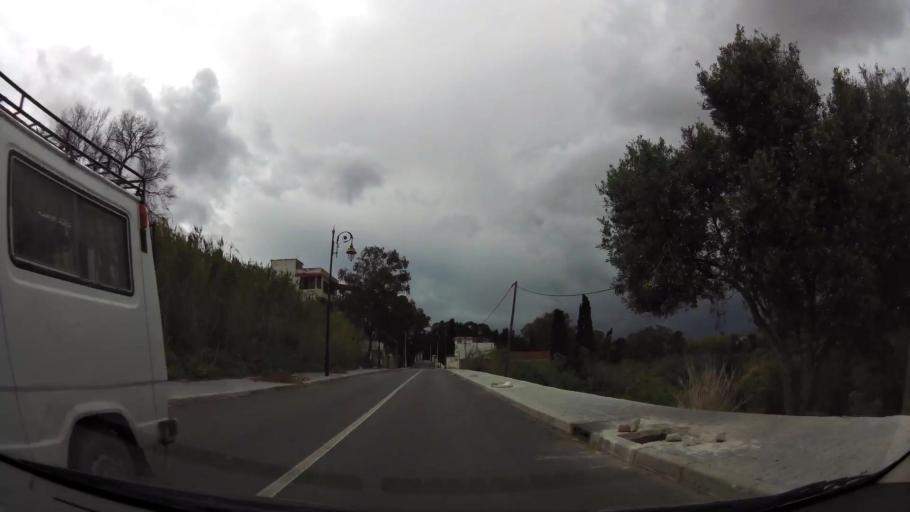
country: MA
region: Tanger-Tetouan
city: Tetouan
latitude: 35.5539
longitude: -5.3577
